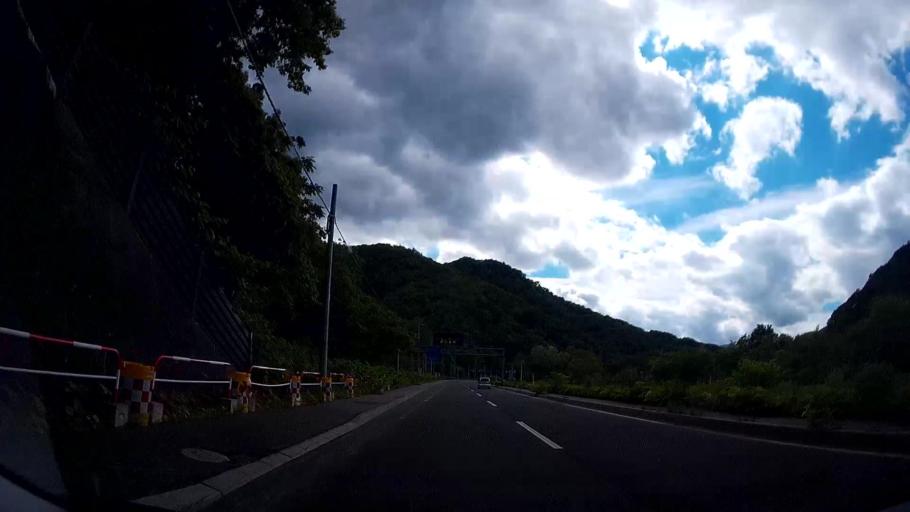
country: JP
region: Hokkaido
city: Sapporo
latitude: 42.9692
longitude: 141.1866
